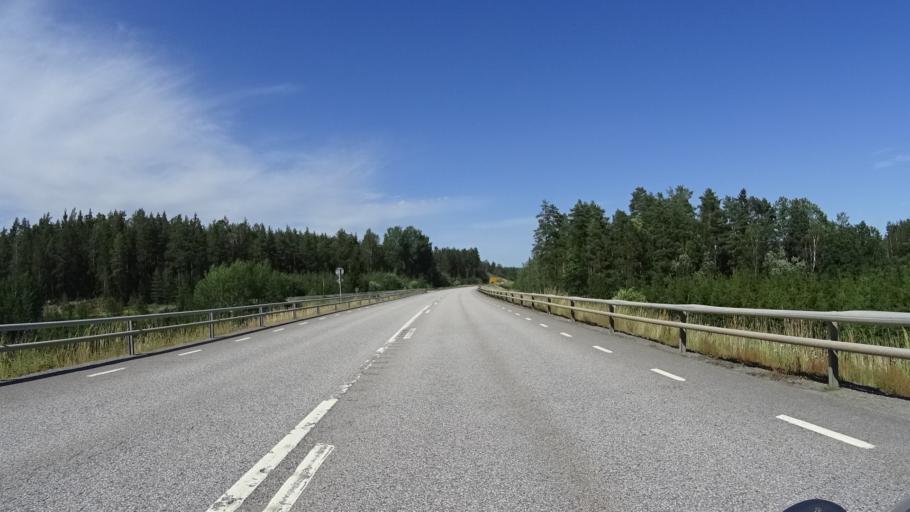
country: SE
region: Kalmar
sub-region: Vasterviks Kommun
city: Gamleby
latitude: 57.9269
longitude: 16.3756
